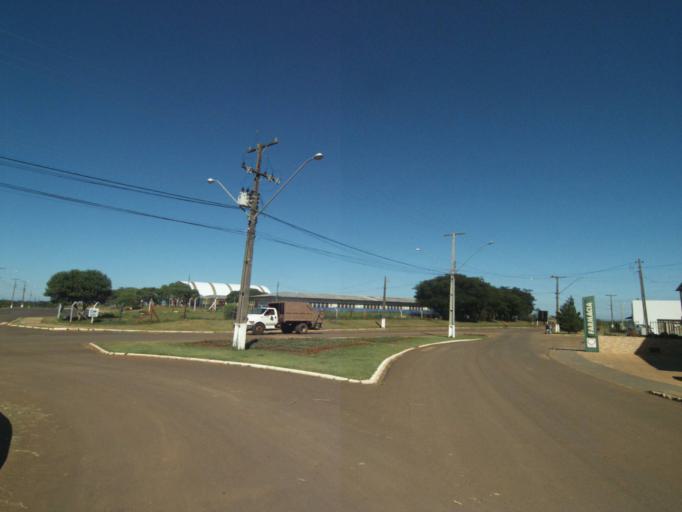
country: BR
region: Parana
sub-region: Pinhao
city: Pinhao
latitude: -25.8341
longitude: -52.0310
